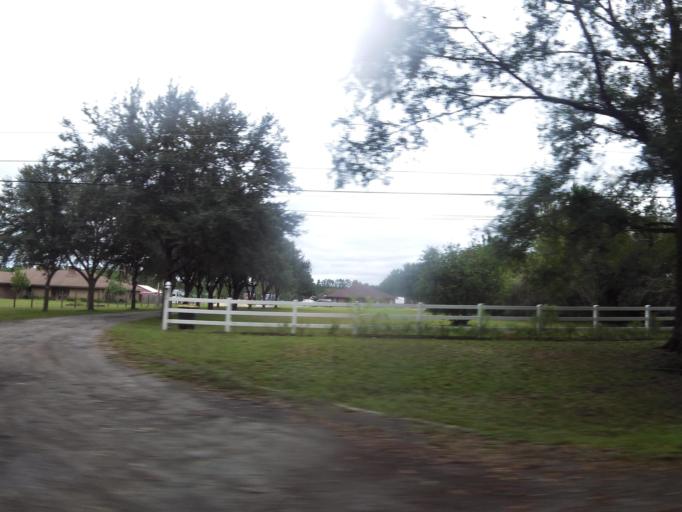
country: US
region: Florida
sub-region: Clay County
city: Lakeside
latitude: 30.2030
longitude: -81.8530
